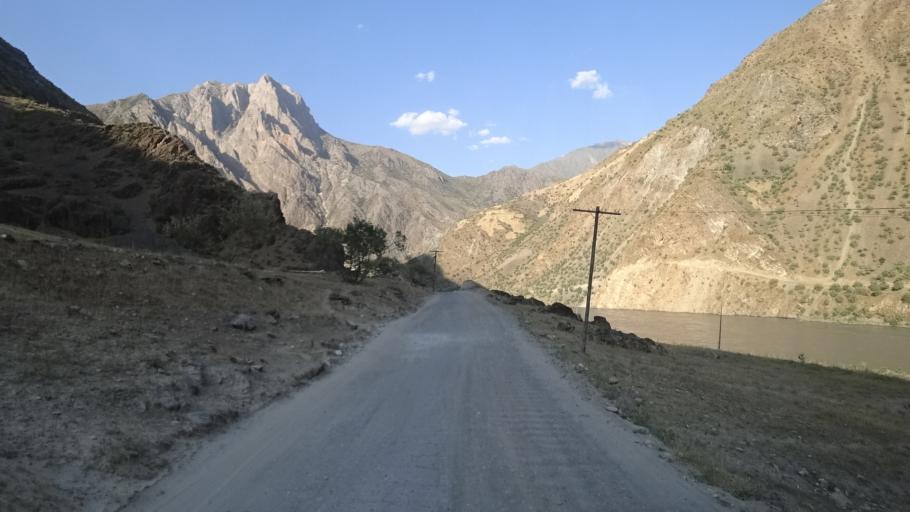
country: AF
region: Badakhshan
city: Maymay
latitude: 38.4805
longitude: 70.9756
